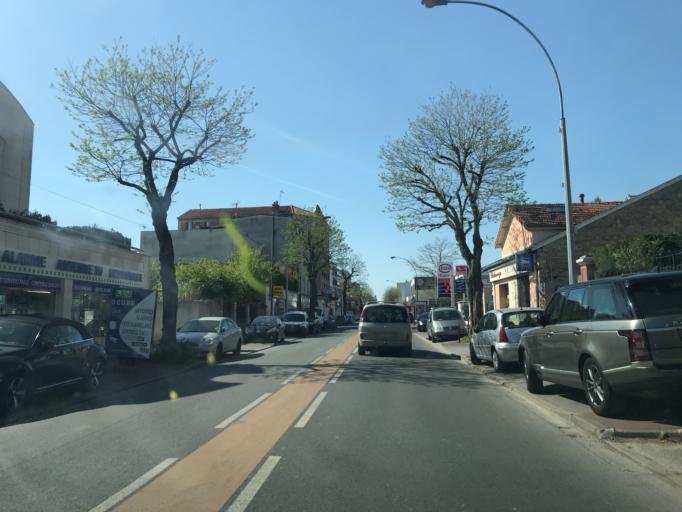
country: FR
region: Ile-de-France
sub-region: Departement du Val-de-Marne
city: Saint-Maur-des-Fosses
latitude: 48.7987
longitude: 2.5008
